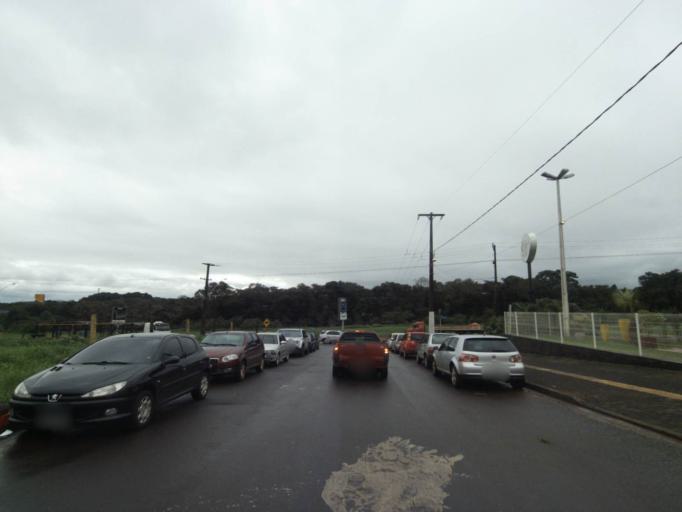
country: PY
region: Alto Parana
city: Ciudad del Este
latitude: -25.5094
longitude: -54.5803
